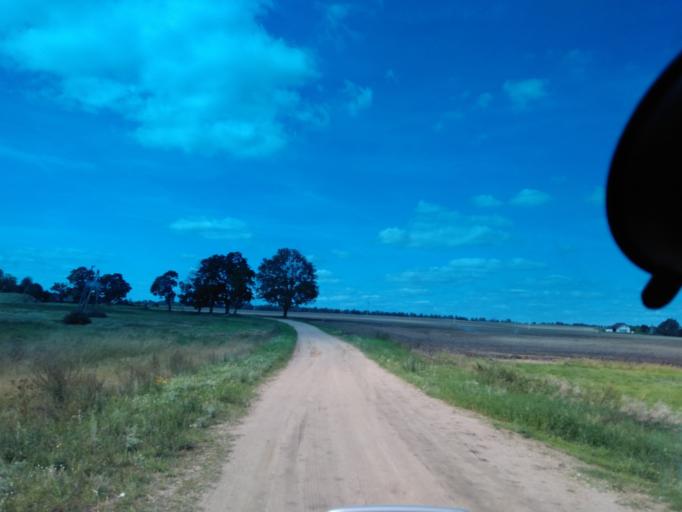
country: BY
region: Minsk
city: Stan'kava
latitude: 53.6341
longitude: 27.3108
